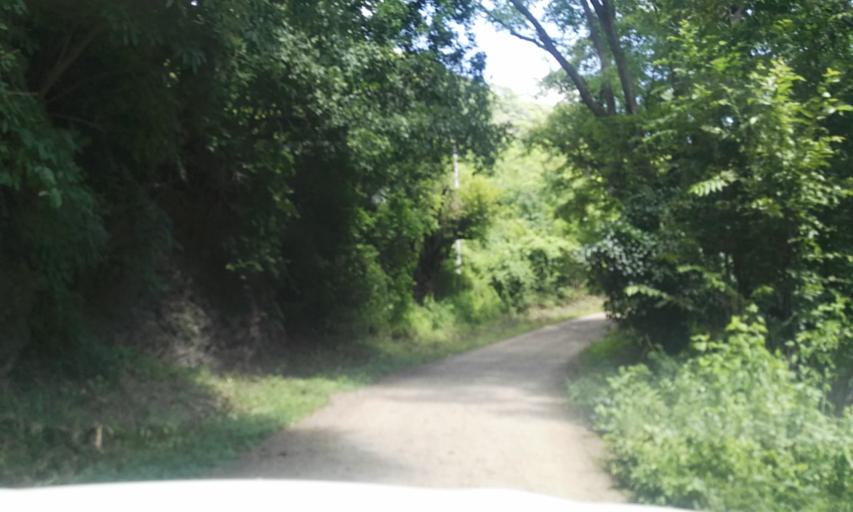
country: NI
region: Matagalpa
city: Terrabona
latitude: 12.7030
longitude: -85.9275
